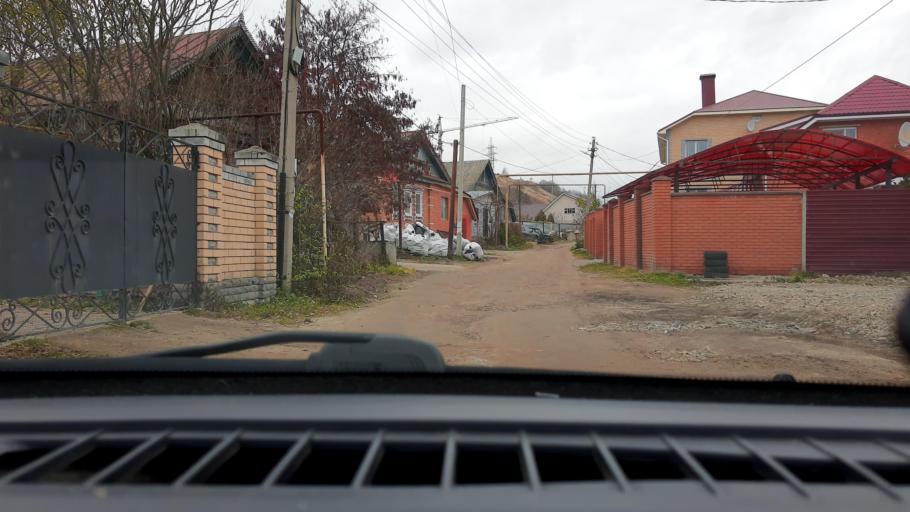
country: RU
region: Nizjnij Novgorod
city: Afonino
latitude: 56.2745
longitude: 44.0992
